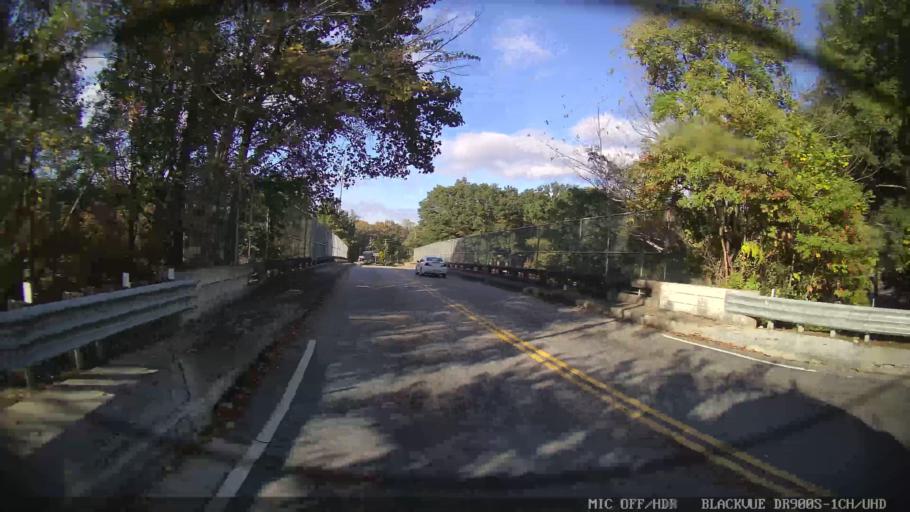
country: US
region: Georgia
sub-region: Fulton County
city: Sandy Springs
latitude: 33.9150
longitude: -84.3903
